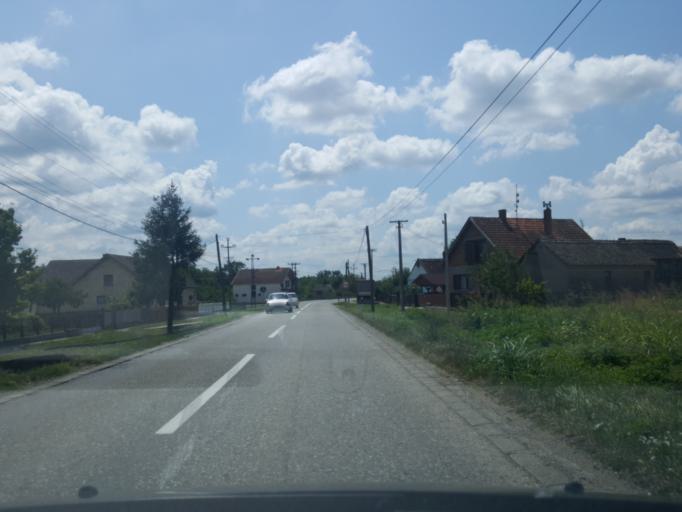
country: RS
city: Glusci
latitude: 44.8801
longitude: 19.5557
